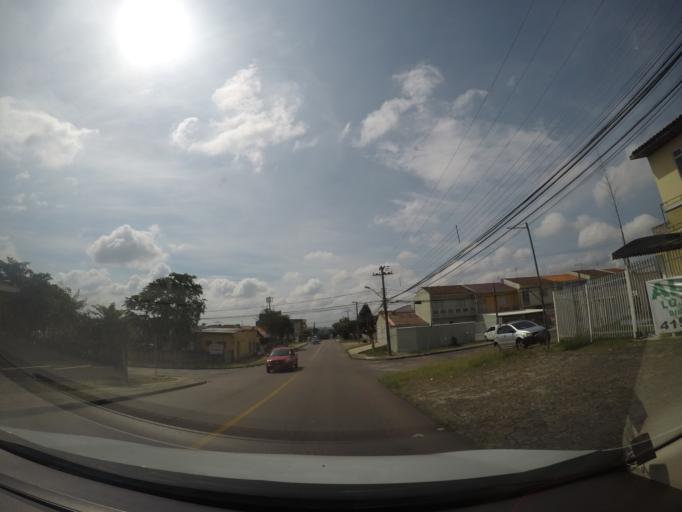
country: BR
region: Parana
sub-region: Curitiba
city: Curitiba
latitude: -25.4908
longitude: -49.2875
